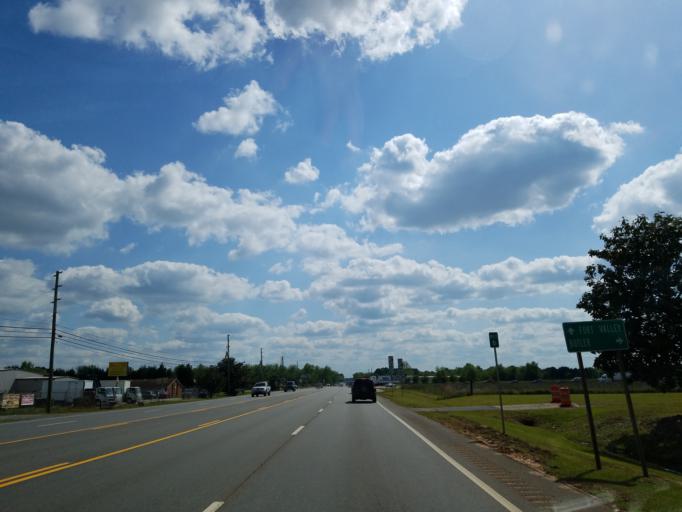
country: US
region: Georgia
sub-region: Peach County
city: Fort Valley
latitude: 32.5779
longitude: -83.8662
